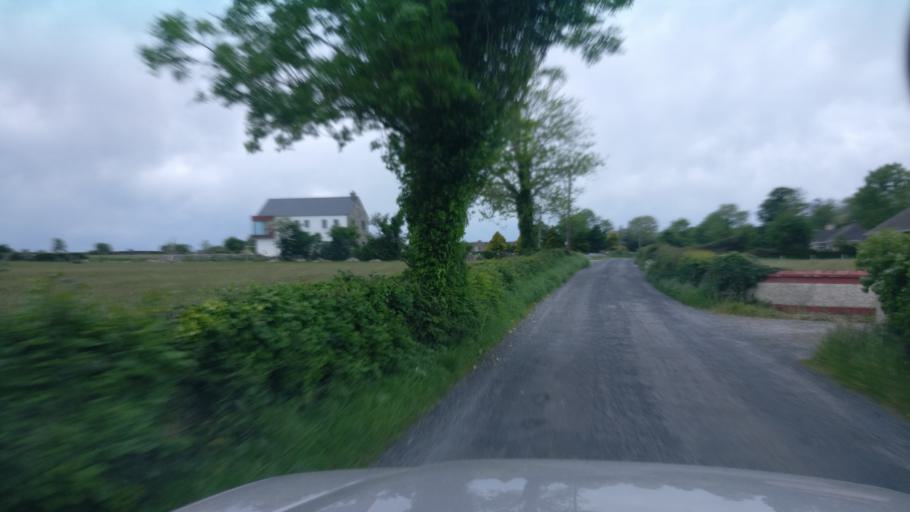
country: IE
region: Connaught
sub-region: County Galway
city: Loughrea
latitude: 53.1756
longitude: -8.4639
